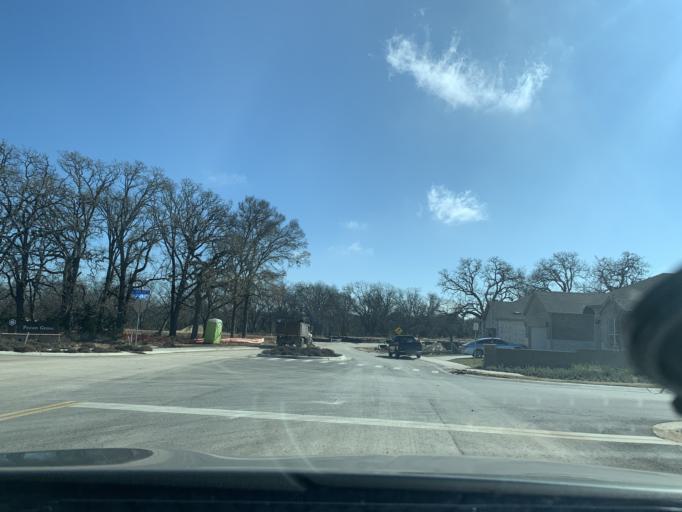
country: US
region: Texas
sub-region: Williamson County
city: Serenada
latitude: 30.7326
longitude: -97.7554
